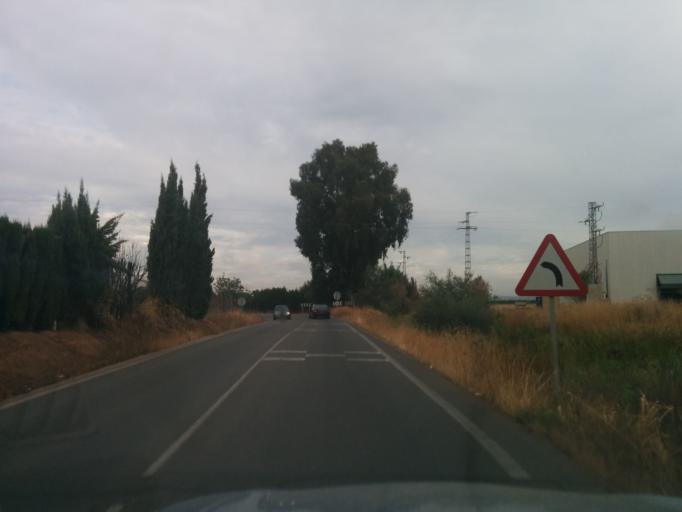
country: ES
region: Andalusia
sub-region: Provincia de Sevilla
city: La Rinconada
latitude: 37.5001
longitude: -6.0137
